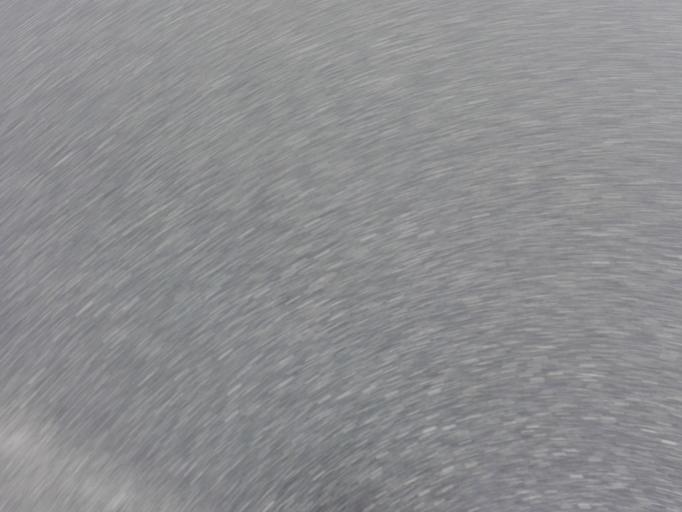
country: FR
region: Pays de la Loire
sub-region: Departement de la Vendee
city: Les Brouzils
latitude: 46.8835
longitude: -1.3198
